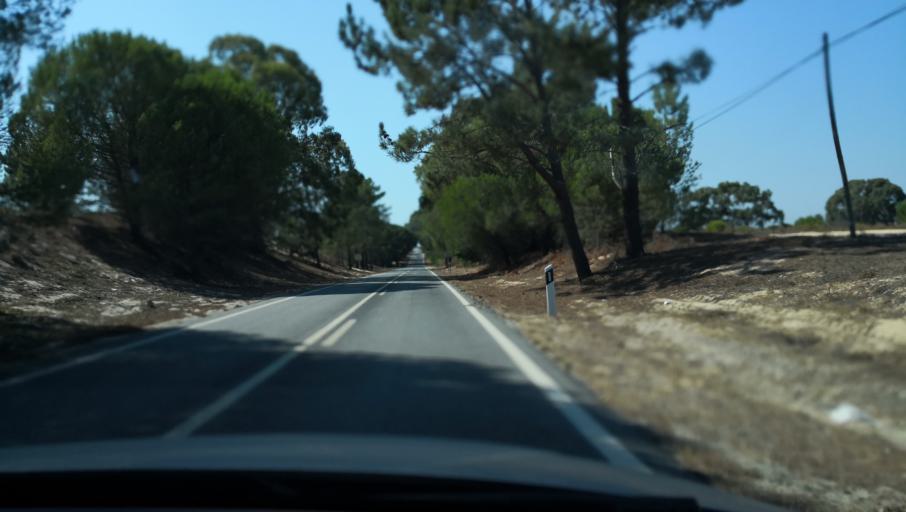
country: PT
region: Setubal
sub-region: Alcacer do Sal
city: Alcacer do Sal
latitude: 38.4057
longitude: -8.7093
